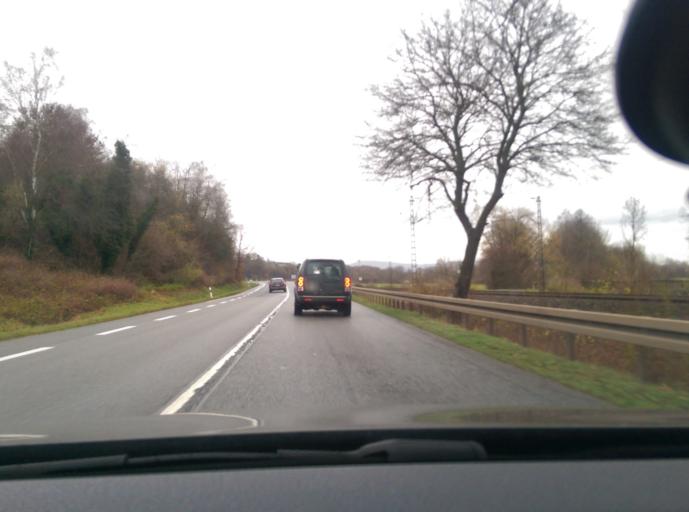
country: DE
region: Hesse
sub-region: Regierungsbezirk Kassel
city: Sontra
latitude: 51.1423
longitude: 9.9775
